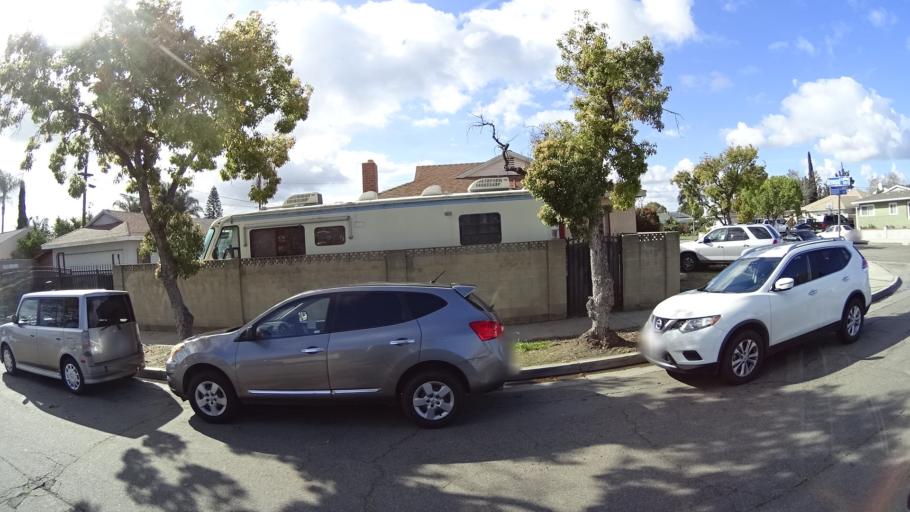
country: US
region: California
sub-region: Orange County
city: Anaheim
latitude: 33.8520
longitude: -117.9004
